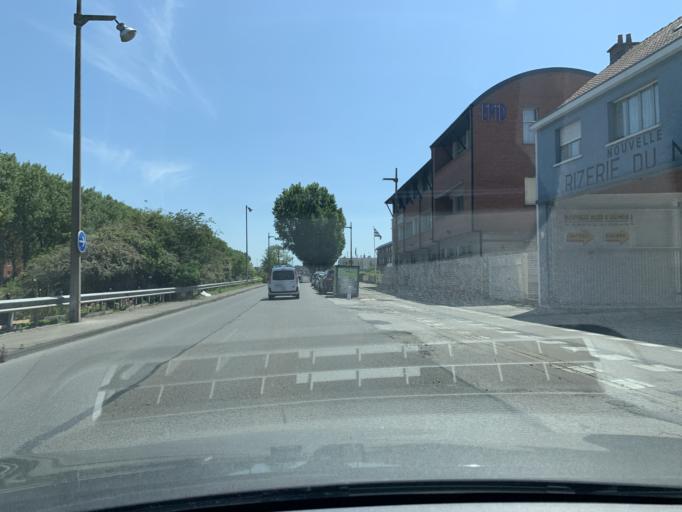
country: FR
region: Nord-Pas-de-Calais
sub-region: Departement du Nord
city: Dunkerque
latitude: 51.0278
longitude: 2.3725
